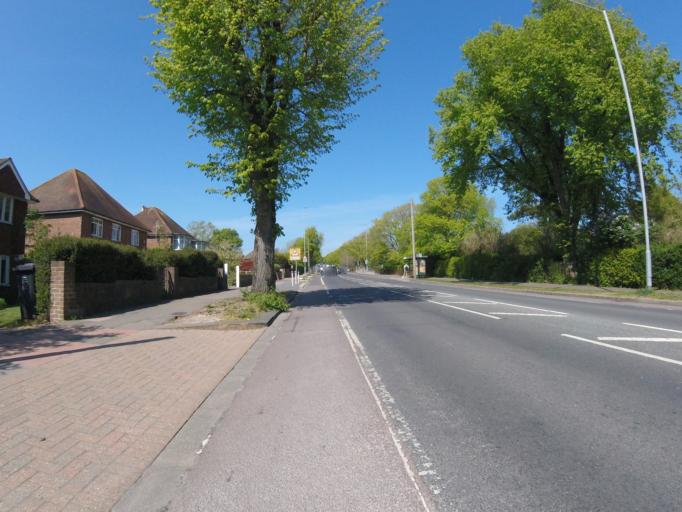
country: GB
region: England
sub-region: Brighton and Hove
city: Brighton
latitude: 50.8483
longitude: -0.1354
